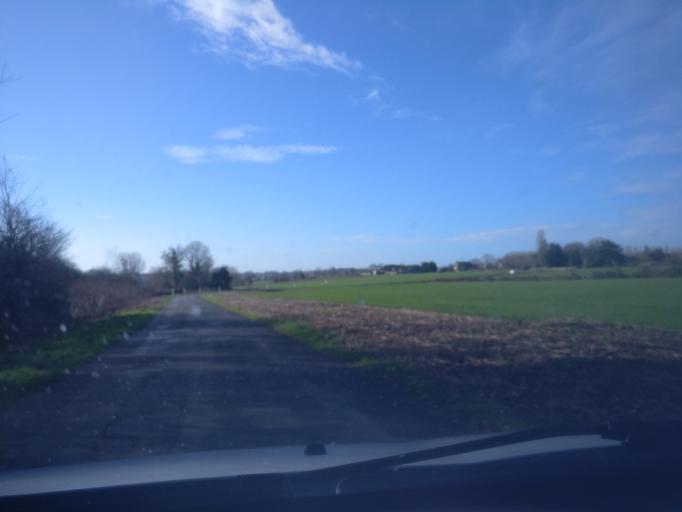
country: FR
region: Lower Normandy
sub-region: Departement de la Manche
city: Pontorson
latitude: 48.5372
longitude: -1.5173
